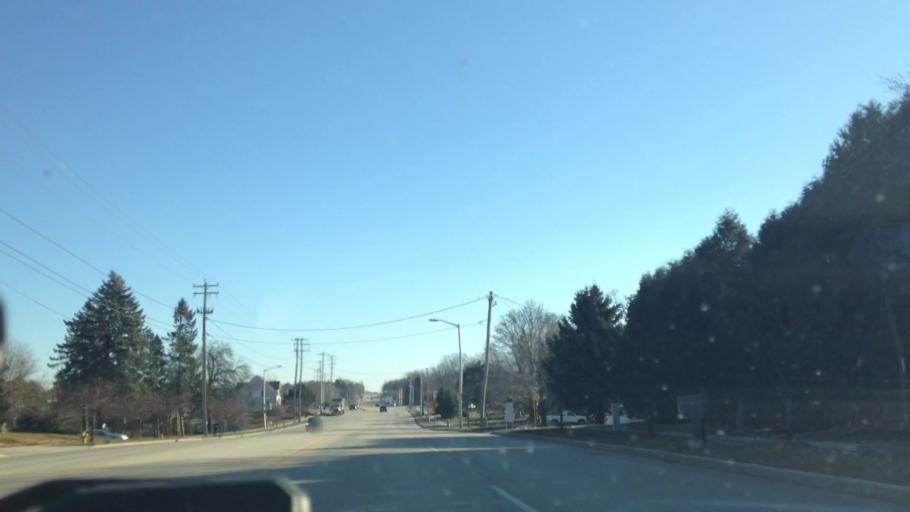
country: US
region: Wisconsin
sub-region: Washington County
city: West Bend
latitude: 43.4268
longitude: -88.1660
